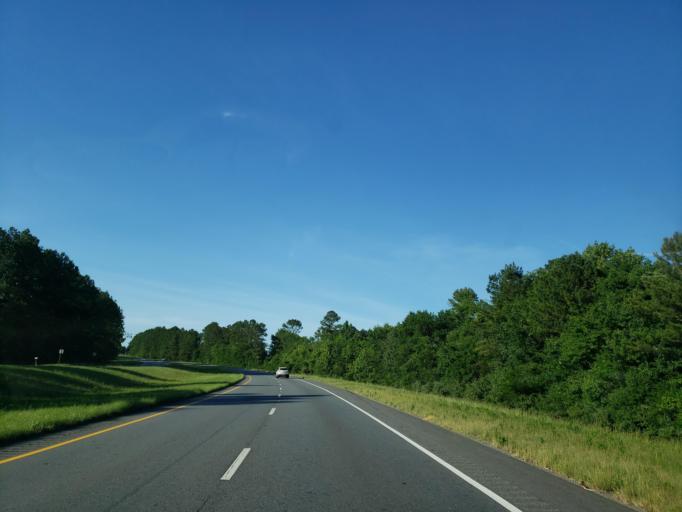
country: US
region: Georgia
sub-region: Floyd County
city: Shannon
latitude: 34.3340
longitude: -85.0810
